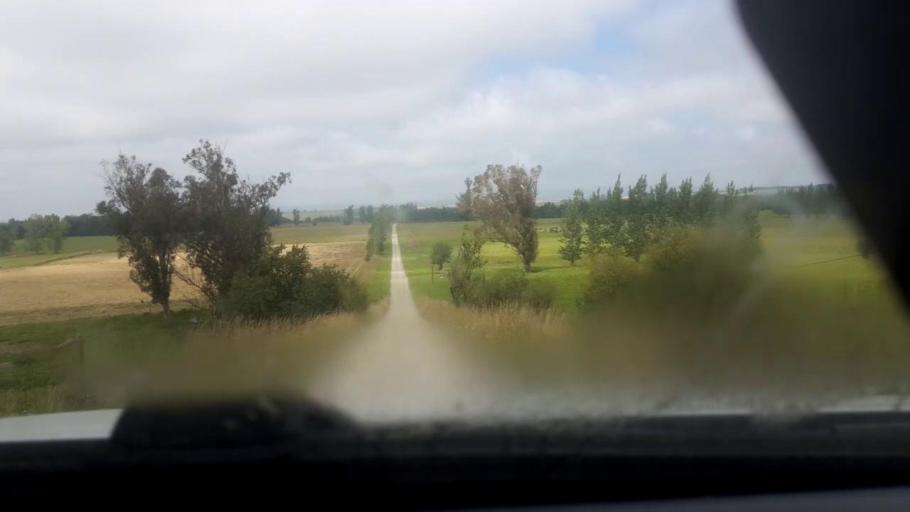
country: NZ
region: Canterbury
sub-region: Timaru District
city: Pleasant Point
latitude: -44.1964
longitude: 171.0914
